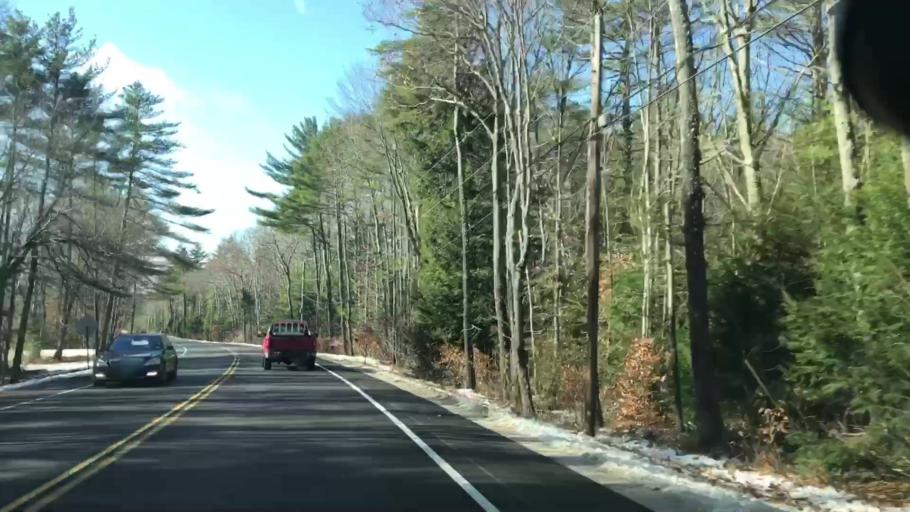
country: US
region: New Hampshire
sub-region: Carroll County
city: Freedom
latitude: 43.7981
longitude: -71.0077
